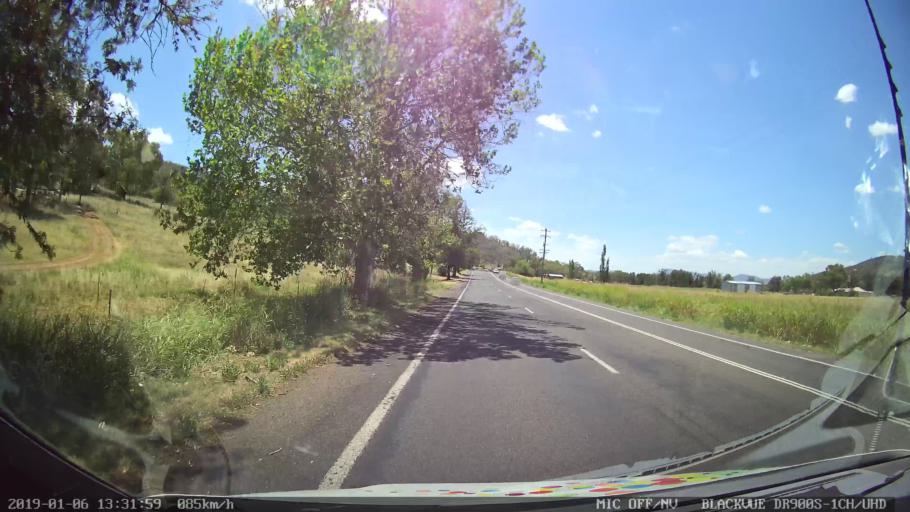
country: AU
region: New South Wales
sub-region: Tamworth Municipality
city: East Tamworth
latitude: -31.1153
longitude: 150.9963
